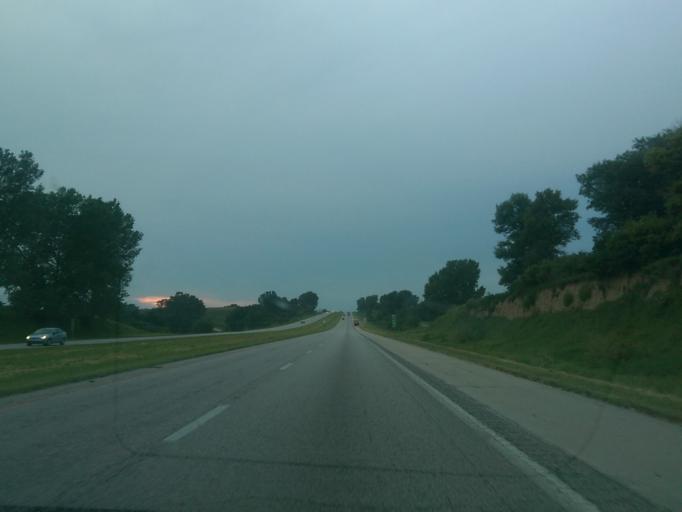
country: US
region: Missouri
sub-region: Holt County
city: Oregon
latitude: 40.0489
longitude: -95.1452
